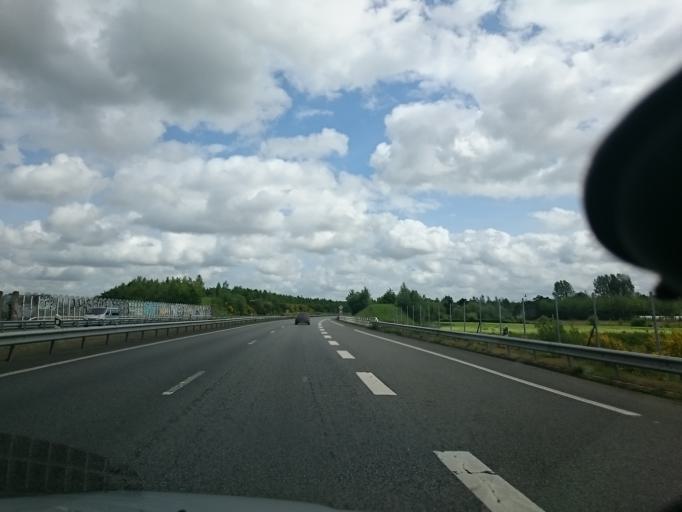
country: FR
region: Brittany
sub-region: Departement d'Ille-et-Vilaine
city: Fouillard
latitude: 48.1372
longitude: -1.5775
